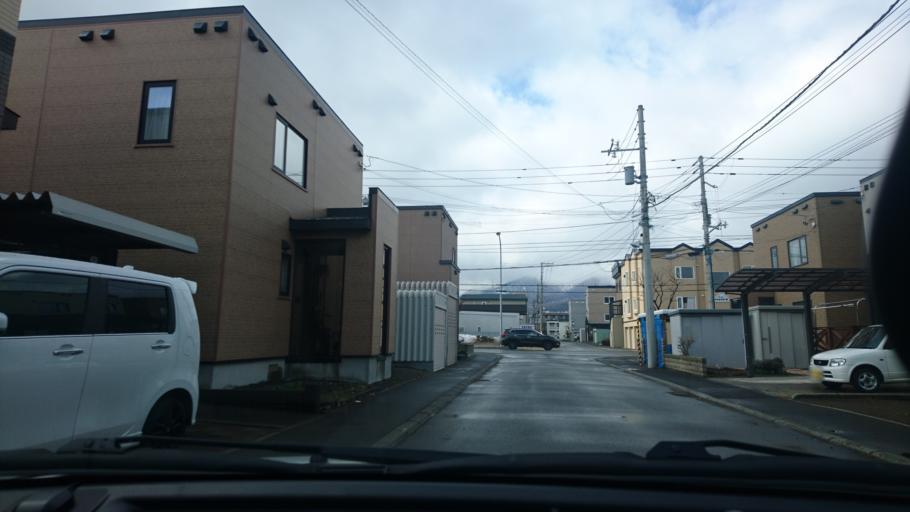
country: JP
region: Hokkaido
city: Sapporo
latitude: 43.1001
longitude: 141.2739
